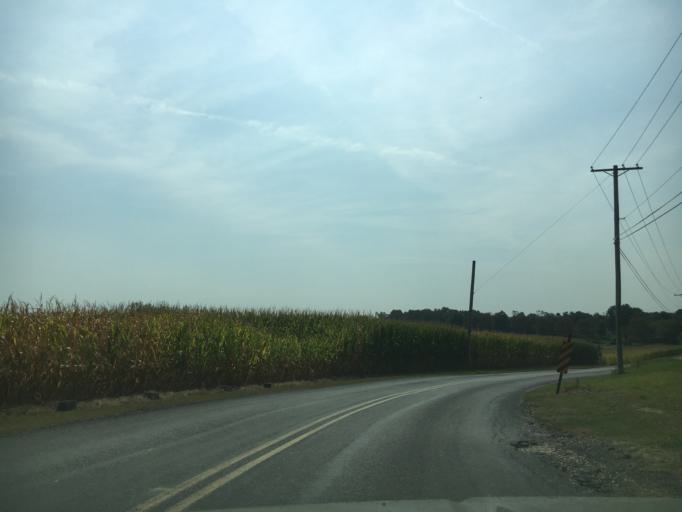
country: US
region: Pennsylvania
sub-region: Berks County
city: Topton
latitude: 40.5549
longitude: -75.7063
